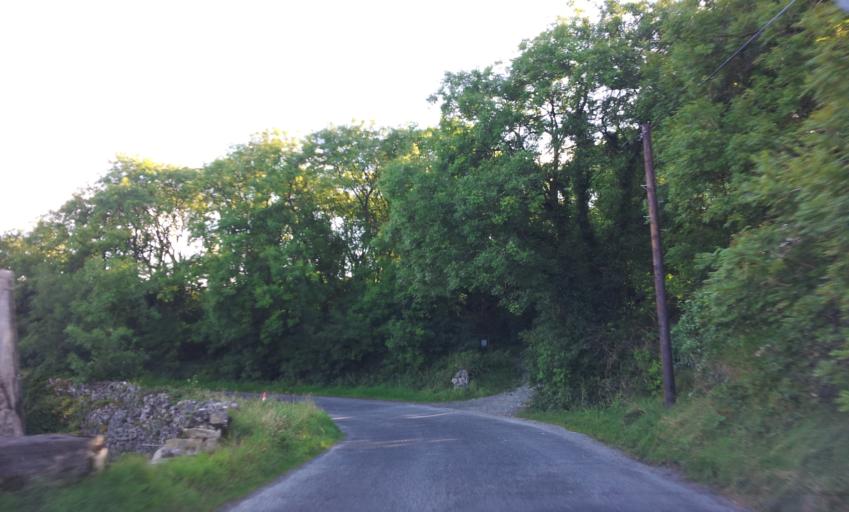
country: IE
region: Connaught
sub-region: County Galway
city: Bearna
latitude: 53.0328
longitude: -9.1366
